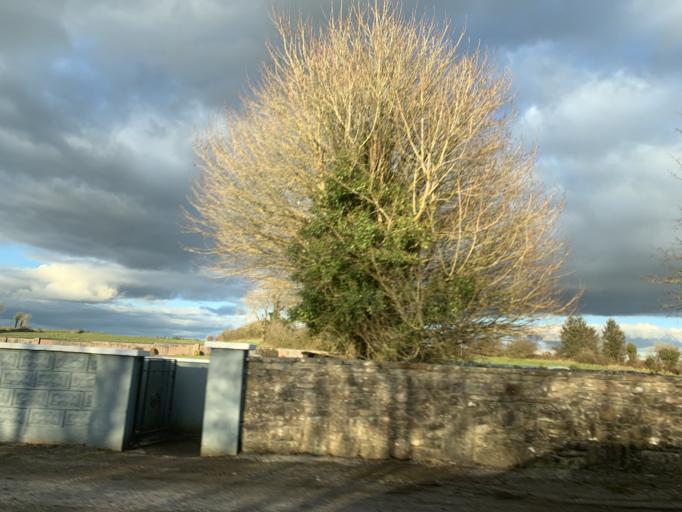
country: IE
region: Connaught
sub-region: Maigh Eo
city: Ballyhaunis
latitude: 53.8104
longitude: -8.6897
